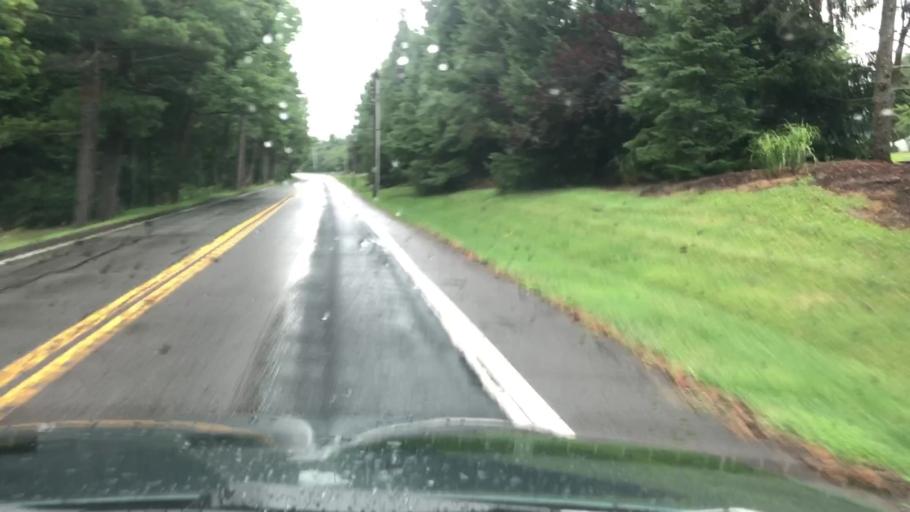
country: US
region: Pennsylvania
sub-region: Monroe County
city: Mountainhome
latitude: 41.2160
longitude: -75.2360
